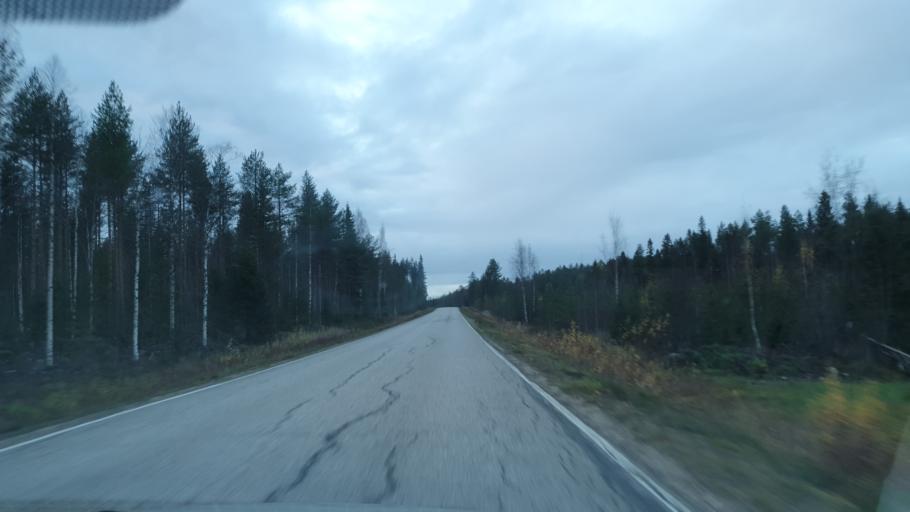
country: FI
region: Kainuu
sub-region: Kajaani
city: Ristijaervi
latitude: 64.4231
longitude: 28.4011
